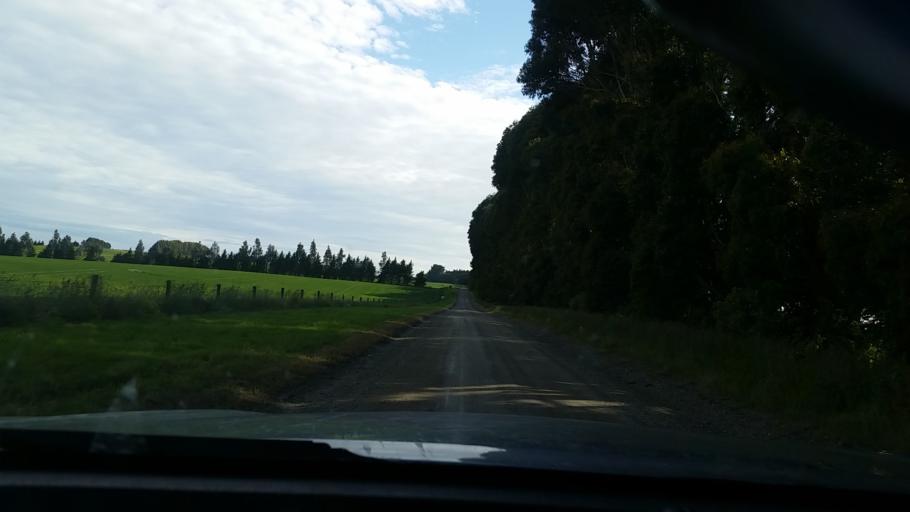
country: NZ
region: Southland
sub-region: Gore District
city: Gore
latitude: -46.2605
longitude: 168.7391
